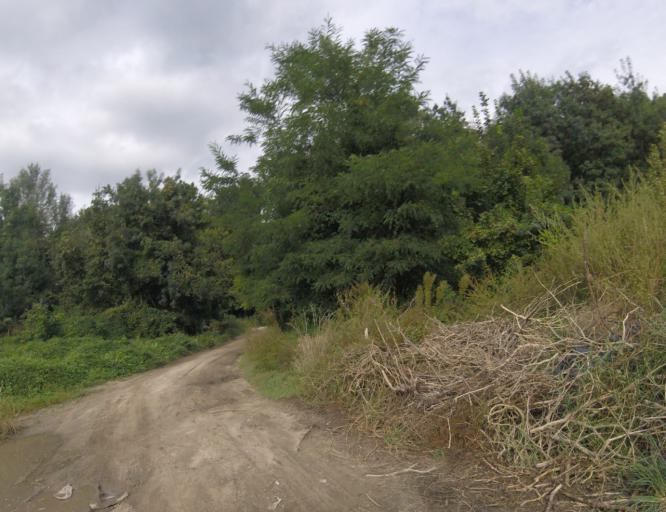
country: HU
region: Pest
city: Szigetcsep
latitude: 47.2823
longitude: 18.9978
